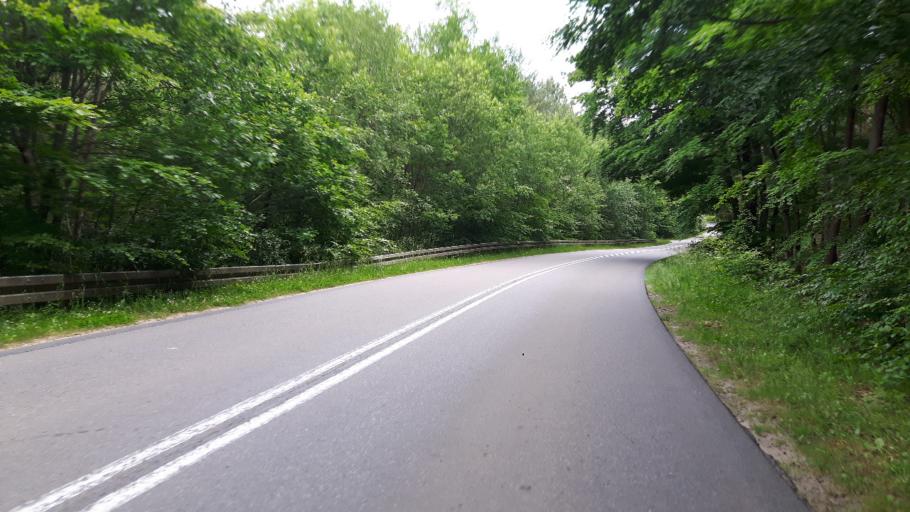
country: PL
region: Pomeranian Voivodeship
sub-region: Powiat leborski
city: Leba
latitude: 54.7540
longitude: 17.6870
